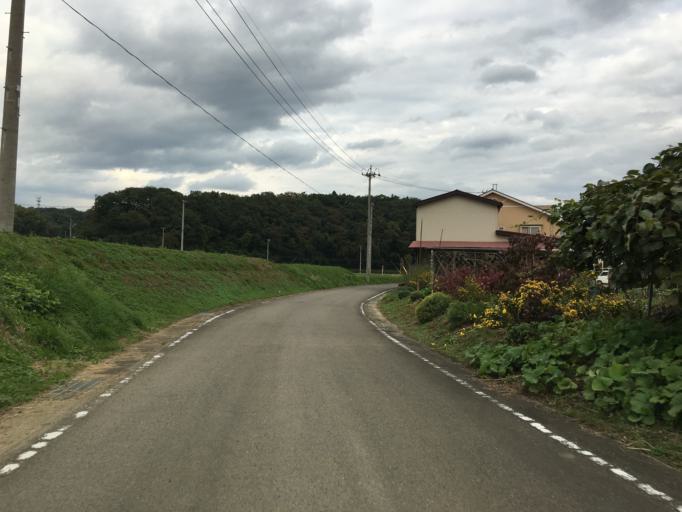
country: JP
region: Fukushima
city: Nihommatsu
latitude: 37.5621
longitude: 140.4044
